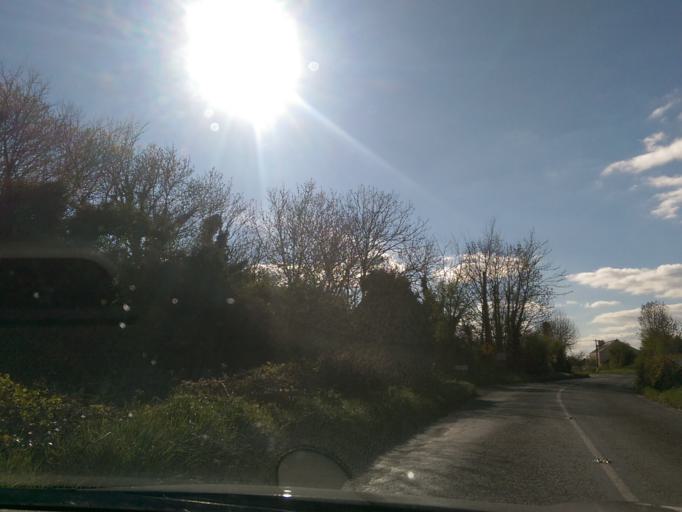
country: IE
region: Leinster
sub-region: Uibh Fhaili
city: Banagher
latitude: 53.1064
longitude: -8.0482
